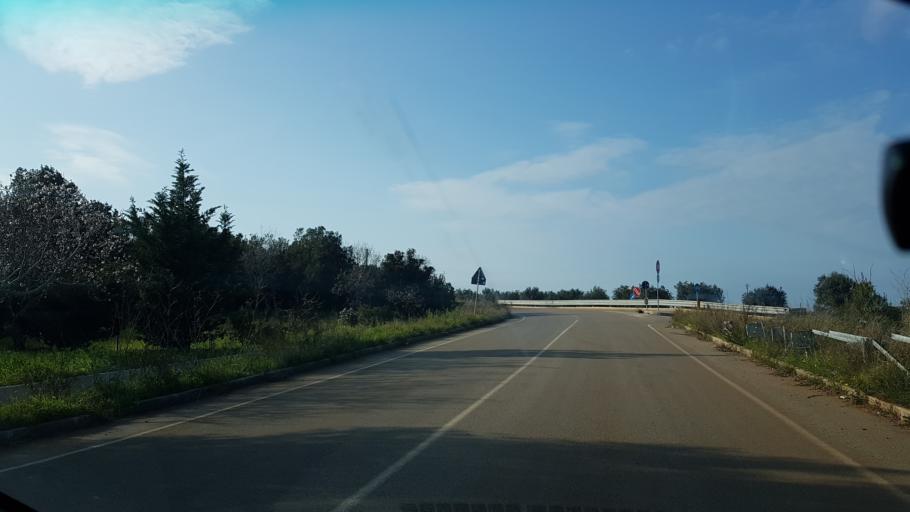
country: IT
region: Apulia
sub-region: Provincia di Brindisi
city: San Vito dei Normanni
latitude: 40.6849
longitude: 17.7754
